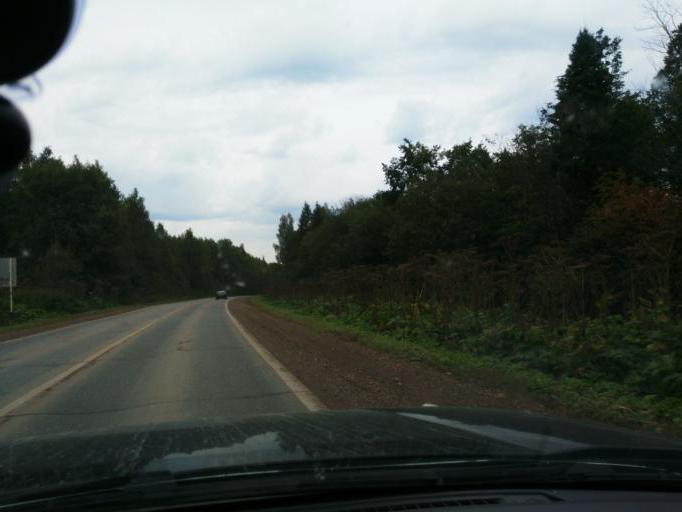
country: RU
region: Perm
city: Chernushka
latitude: 56.6773
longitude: 56.1719
